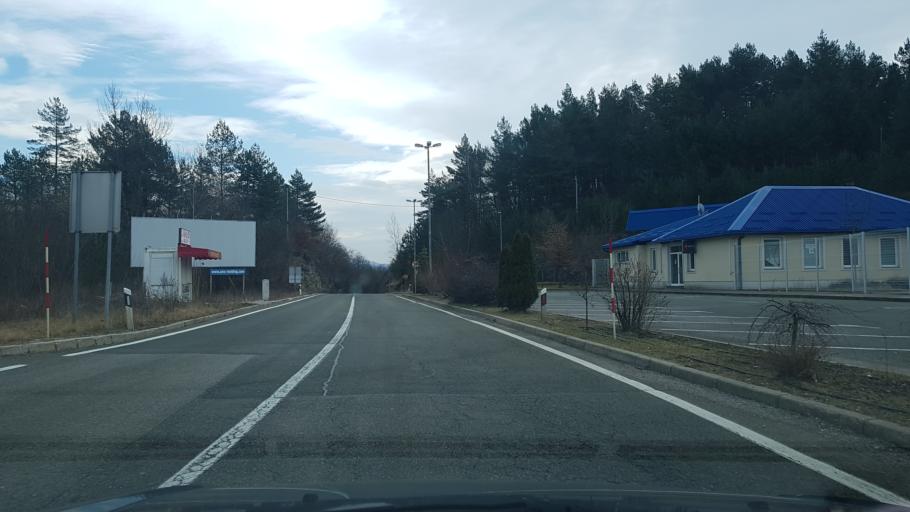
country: SI
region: Ilirska Bistrica
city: Ilirska Bistrica
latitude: 45.4919
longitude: 14.2185
